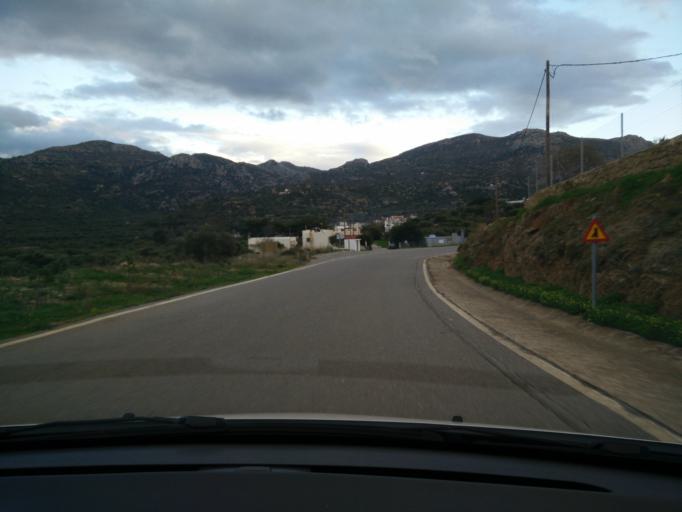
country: GR
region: Crete
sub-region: Nomos Lasithiou
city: Gra Liyia
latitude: 35.0854
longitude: 25.7073
